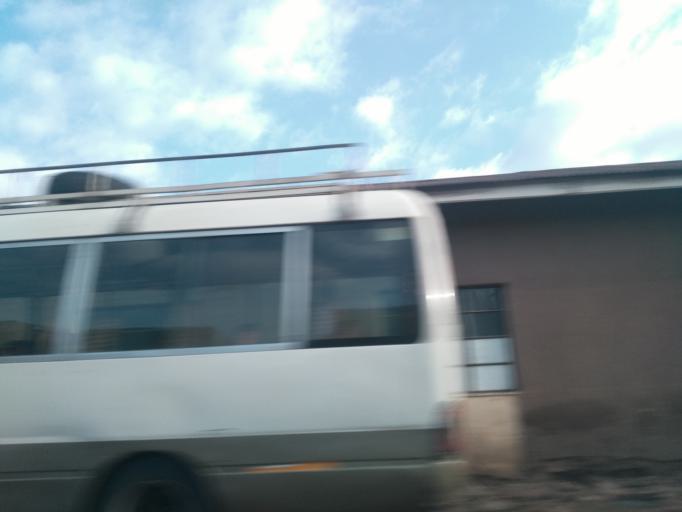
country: TZ
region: Arusha
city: Arusha
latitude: -3.3685
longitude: 36.6820
